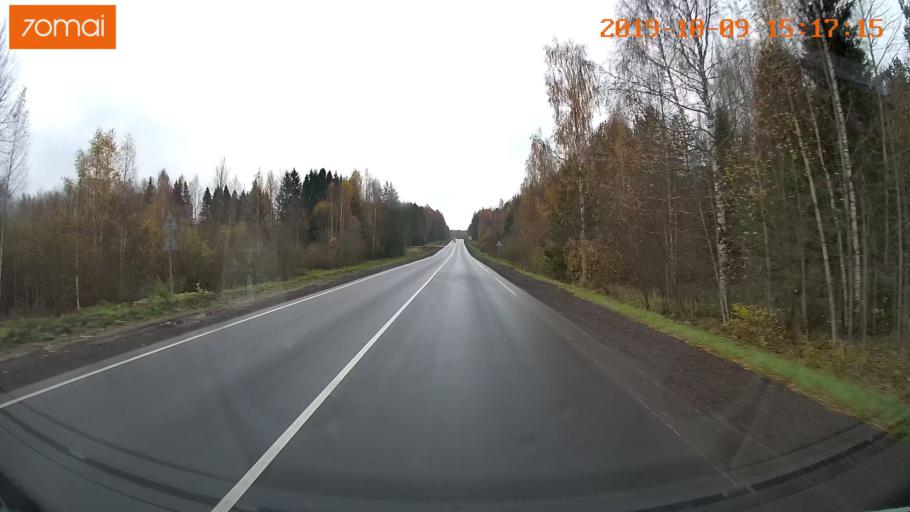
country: RU
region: Kostroma
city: Susanino
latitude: 58.1008
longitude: 41.5834
